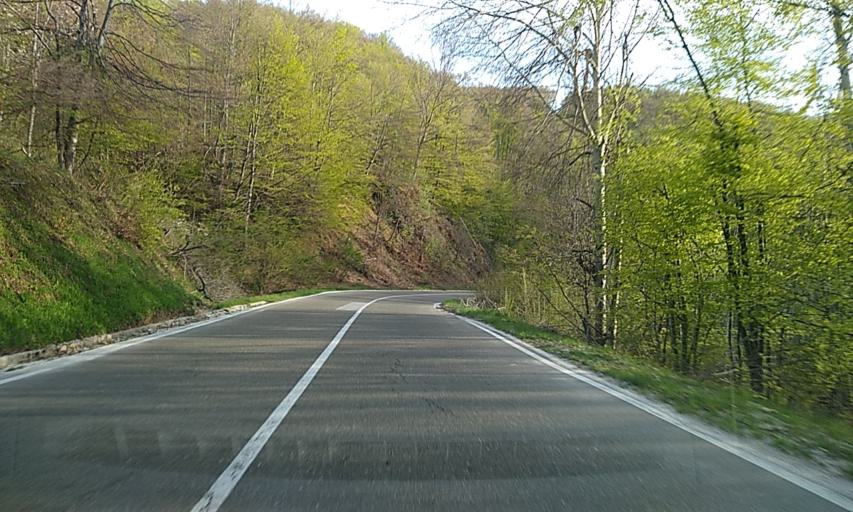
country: RS
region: Central Serbia
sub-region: Pcinjski Okrug
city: Surdulica
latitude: 42.6653
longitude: 22.3084
